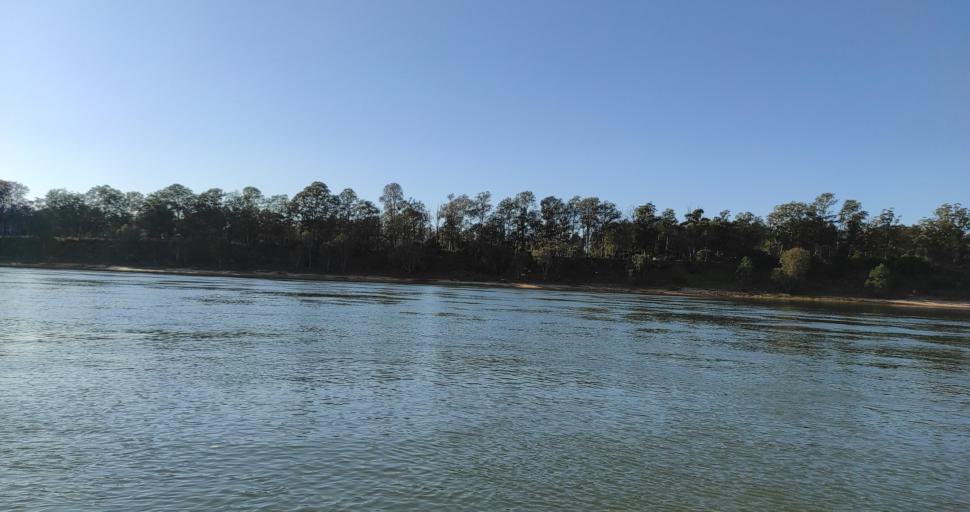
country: AR
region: Corrientes
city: Ituzaingo
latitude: -27.6042
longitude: -56.8245
